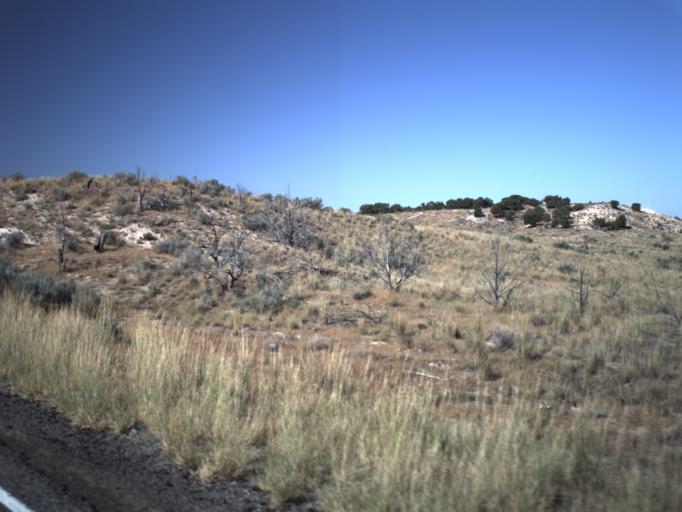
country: US
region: Utah
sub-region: Juab County
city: Mona
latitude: 39.7553
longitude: -112.1813
